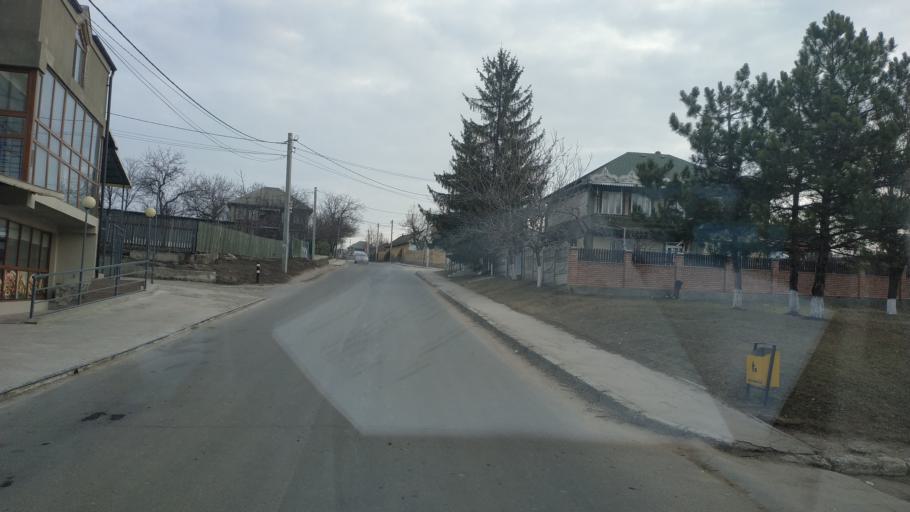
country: MD
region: Chisinau
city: Singera
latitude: 46.9637
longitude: 29.0564
